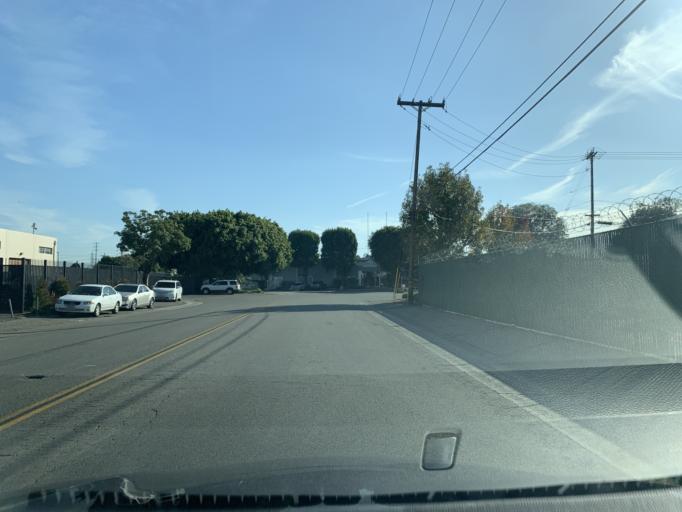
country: US
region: California
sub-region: Orange County
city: Anaheim
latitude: 33.8141
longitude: -117.9043
